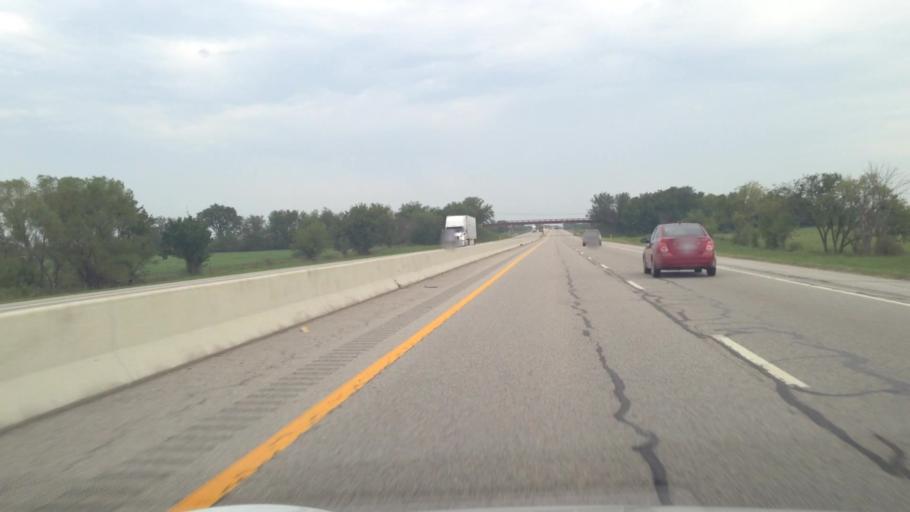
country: US
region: Oklahoma
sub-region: Ottawa County
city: Fairland
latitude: 36.7608
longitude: -94.8991
